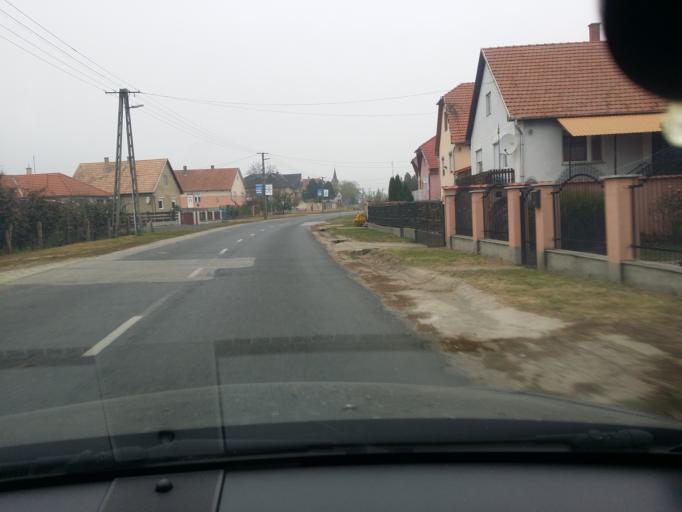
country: HU
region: Szabolcs-Szatmar-Bereg
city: Kek
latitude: 48.1104
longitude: 21.8808
